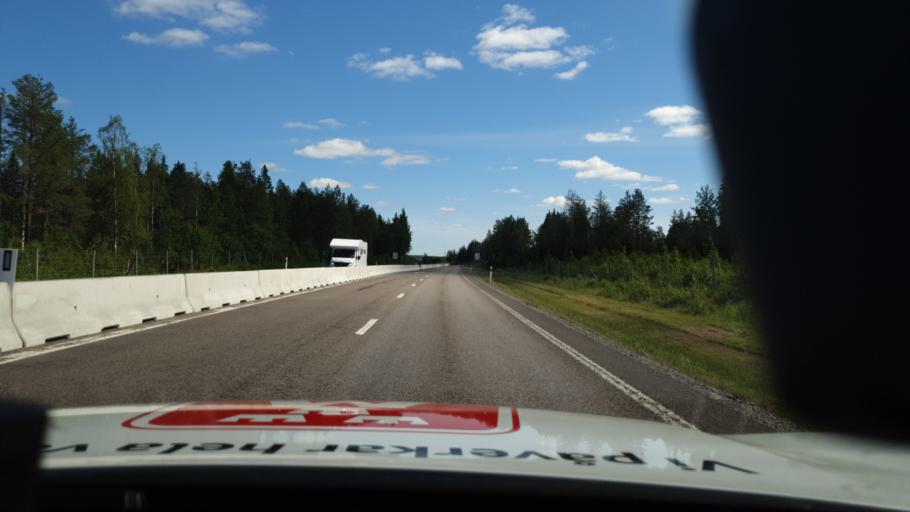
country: SE
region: Norrbotten
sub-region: Kalix Kommun
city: Toere
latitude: 65.9082
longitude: 22.8328
